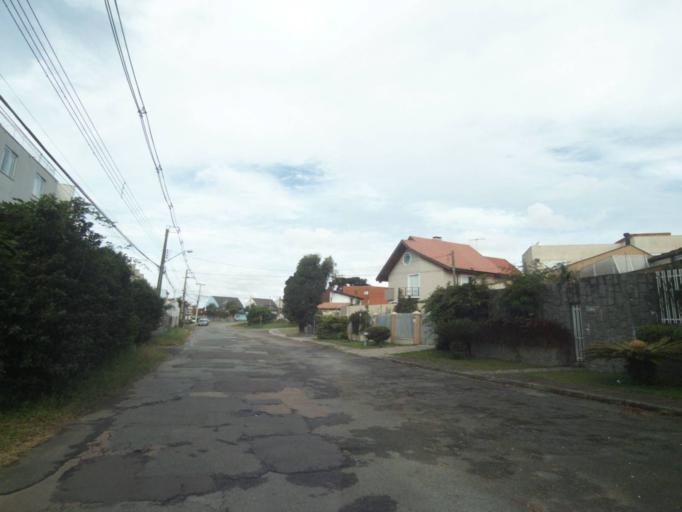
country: BR
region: Parana
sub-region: Curitiba
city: Curitiba
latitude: -25.4385
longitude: -49.3037
